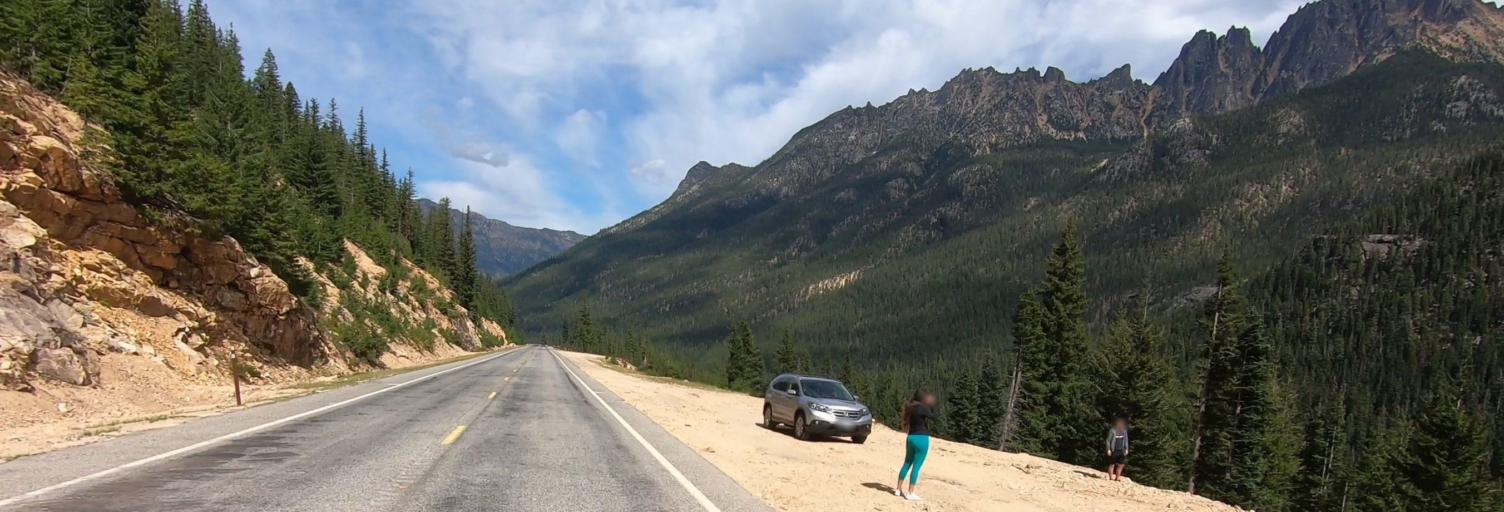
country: US
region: Washington
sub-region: Chelan County
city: Granite Falls
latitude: 48.5388
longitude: -120.6358
